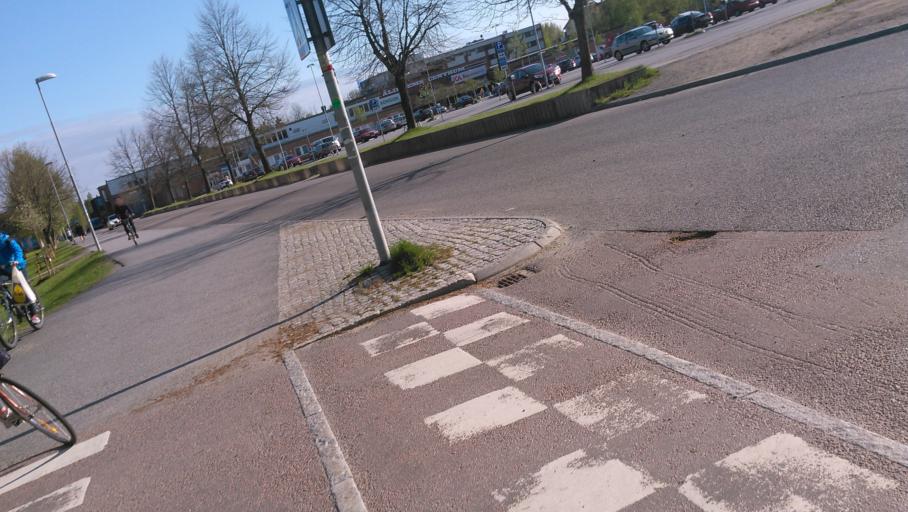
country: SE
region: Vaesterbotten
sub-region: Umea Kommun
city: Umea
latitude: 63.8139
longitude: 20.3162
